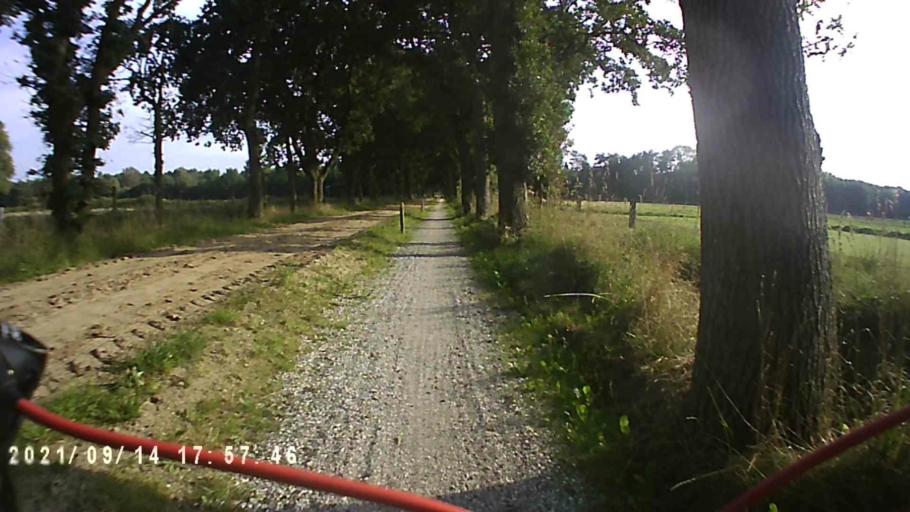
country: NL
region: Drenthe
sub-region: Gemeente Tynaarlo
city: Zuidlaren
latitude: 53.1274
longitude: 6.6477
